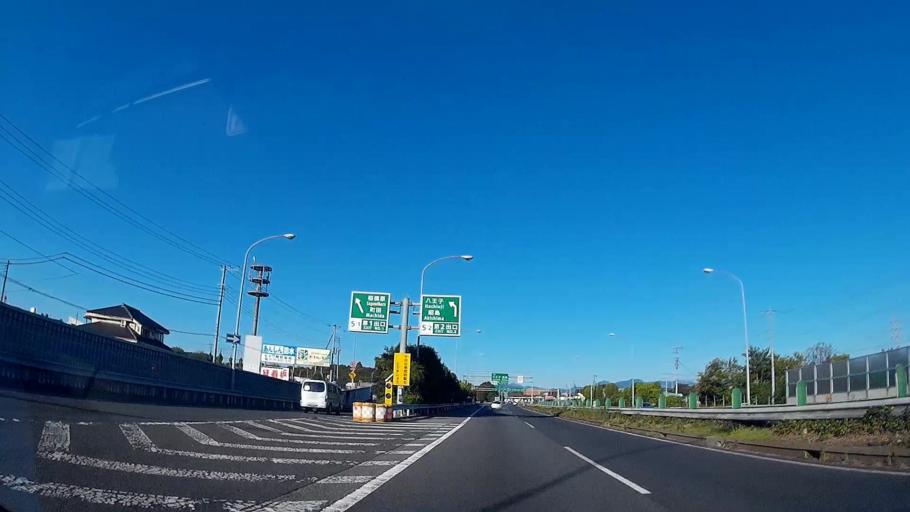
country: JP
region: Tokyo
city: Hachioji
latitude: 35.6749
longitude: 139.3564
